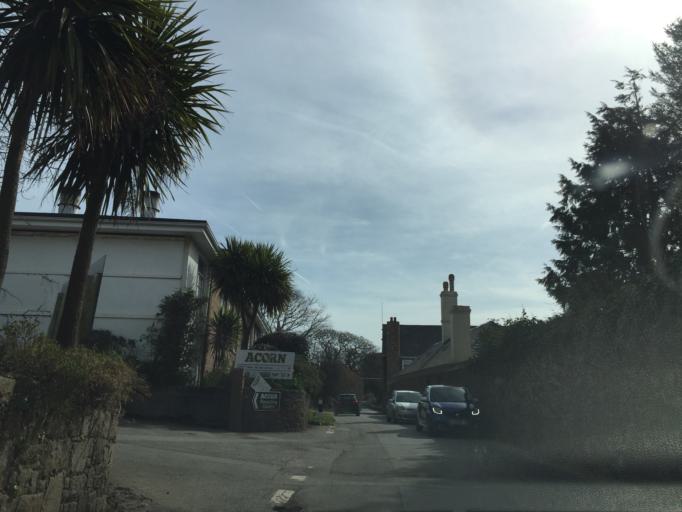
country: JE
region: St Helier
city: Saint Helier
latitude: 49.2337
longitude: -2.0949
